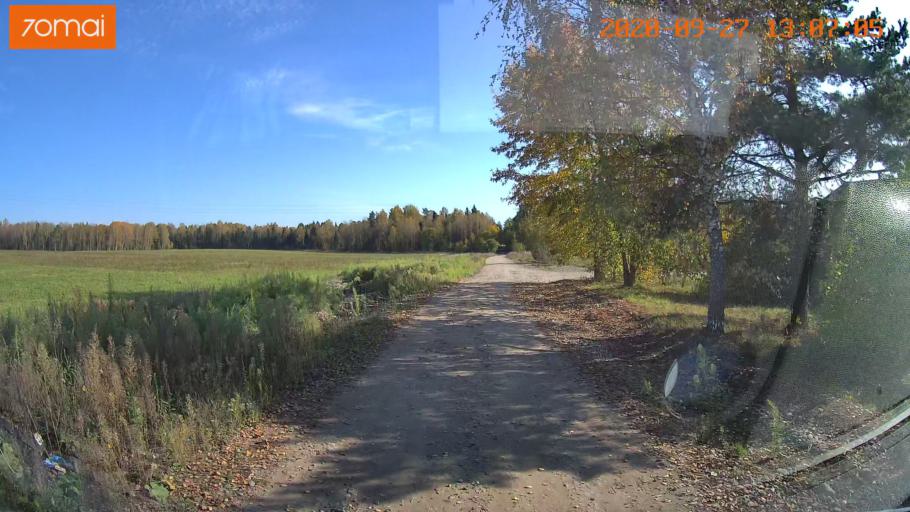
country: RU
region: Ivanovo
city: Furmanov
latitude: 57.1646
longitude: 41.0733
